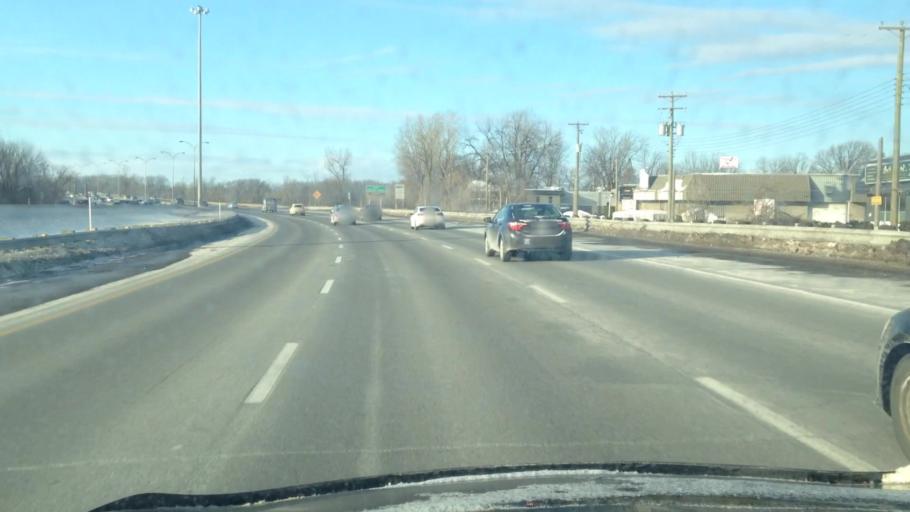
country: CA
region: Quebec
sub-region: Laurentides
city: Boisbriand
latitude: 45.6048
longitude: -73.8059
